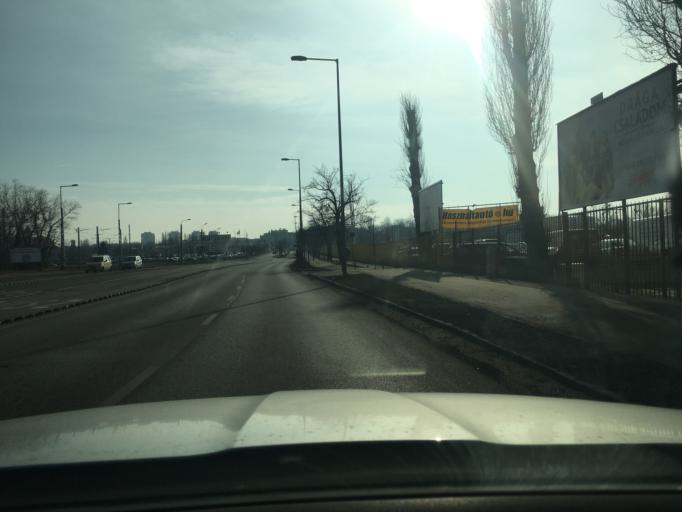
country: HU
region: Budapest
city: Budapest X. keruelet
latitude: 47.4966
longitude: 19.1378
